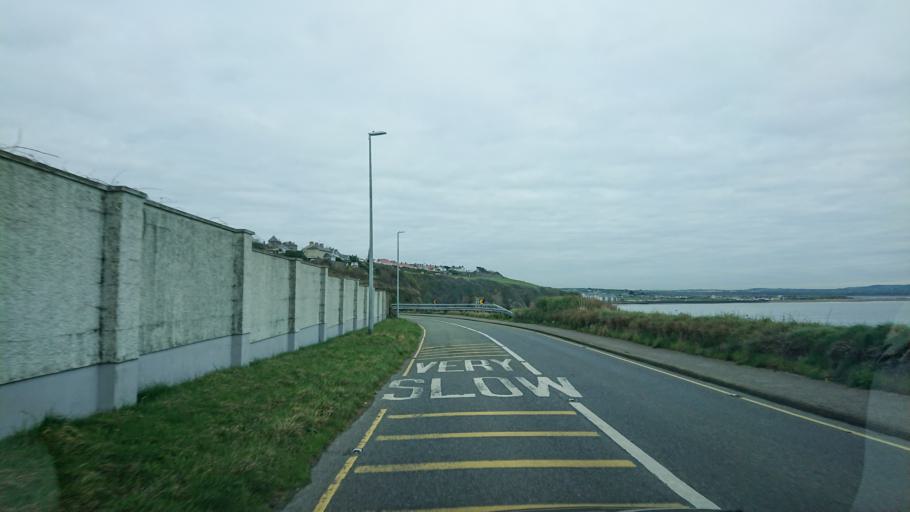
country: IE
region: Munster
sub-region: Waterford
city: Tra Mhor
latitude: 52.1523
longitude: -7.1602
